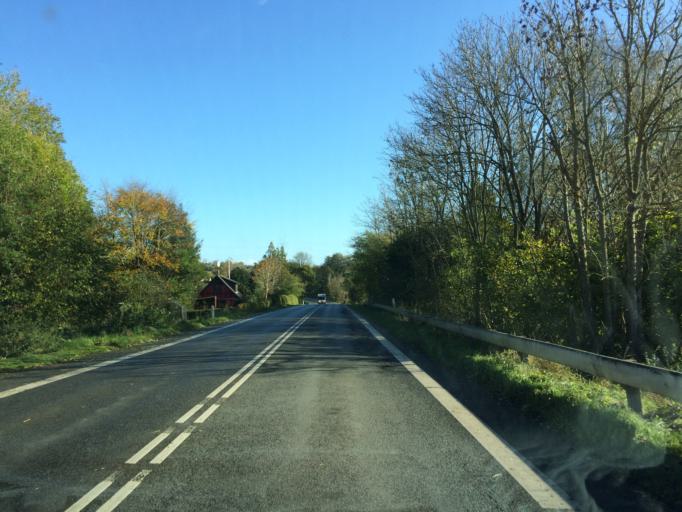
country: DK
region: South Denmark
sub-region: Fredericia Kommune
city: Taulov
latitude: 55.5298
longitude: 9.5715
